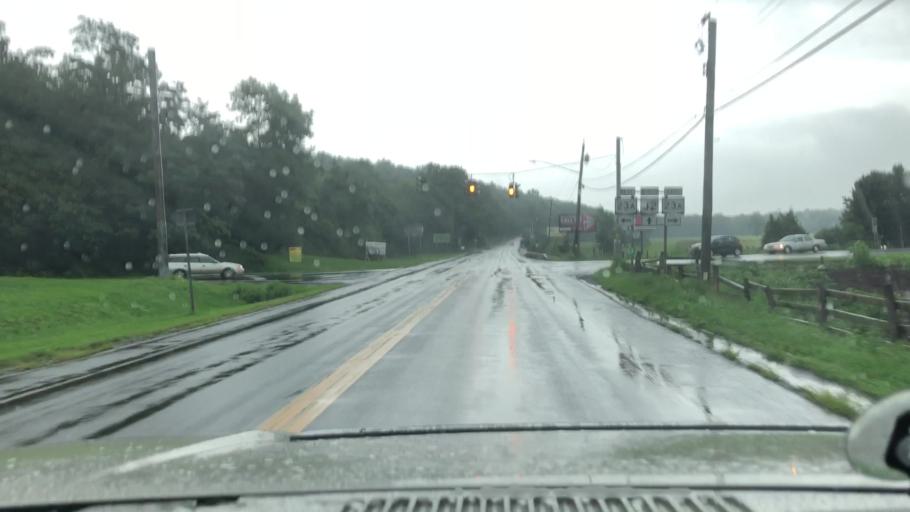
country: US
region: New York
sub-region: Greene County
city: Palenville
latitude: 42.1921
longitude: -73.9857
